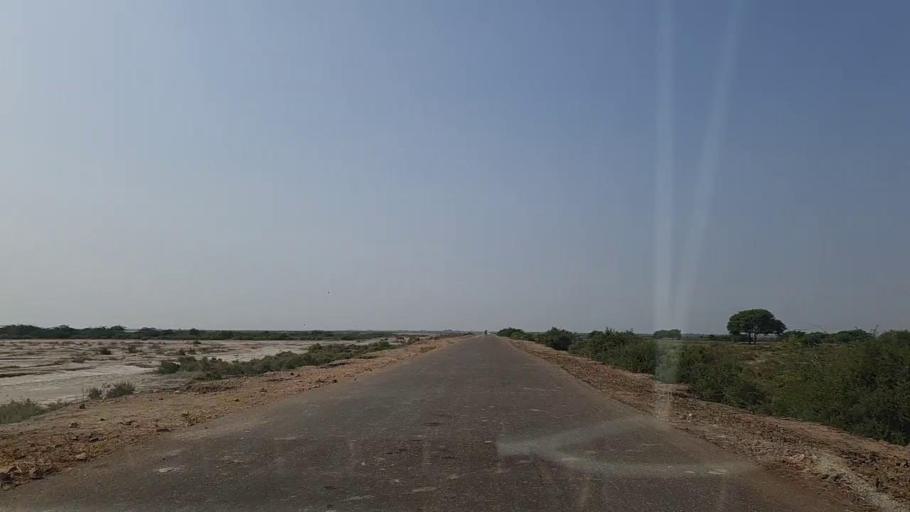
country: PK
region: Sindh
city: Chuhar Jamali
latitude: 24.2217
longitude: 67.8975
